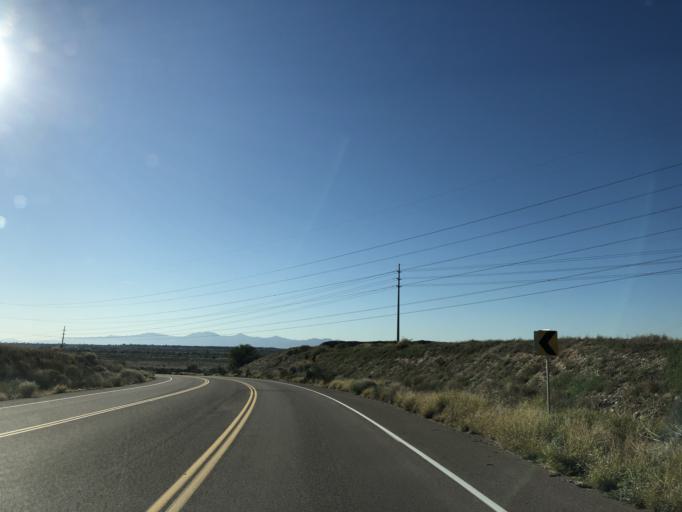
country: US
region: Arizona
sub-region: Maricopa County
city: Sun City West
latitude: 33.6961
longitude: -112.2912
